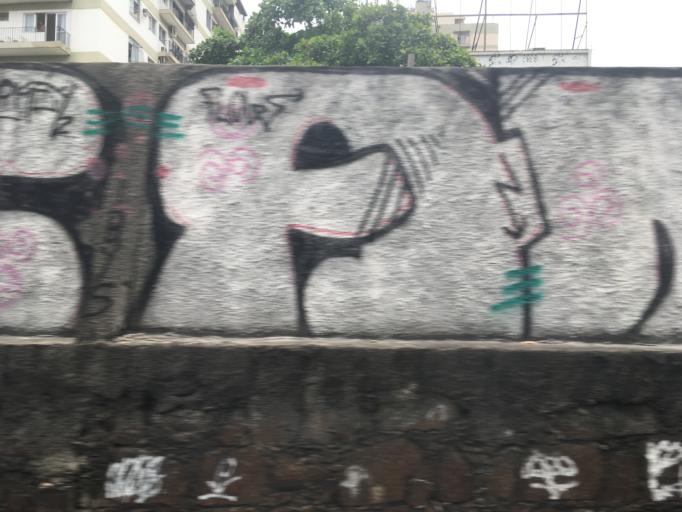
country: BR
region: Rio de Janeiro
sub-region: Rio De Janeiro
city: Rio de Janeiro
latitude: -22.9015
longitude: -43.2476
